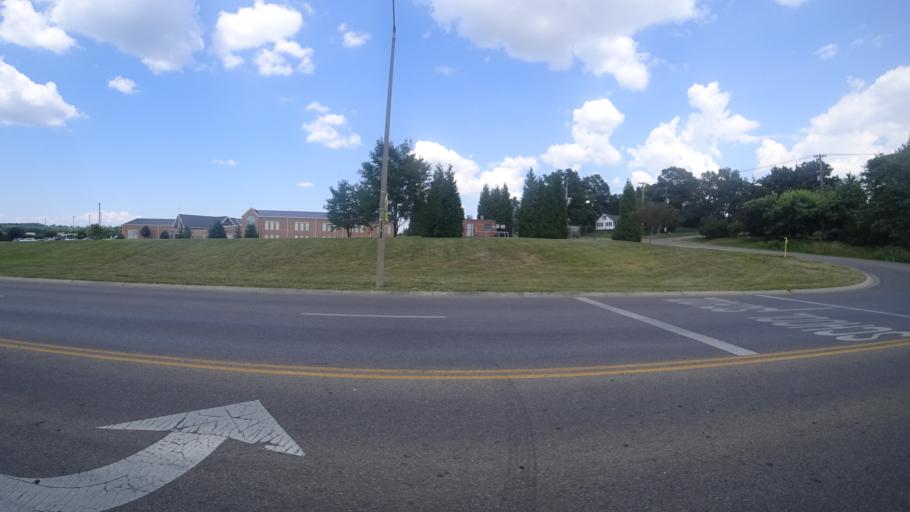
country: US
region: Ohio
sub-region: Butler County
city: New Miami
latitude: 39.4215
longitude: -84.5529
